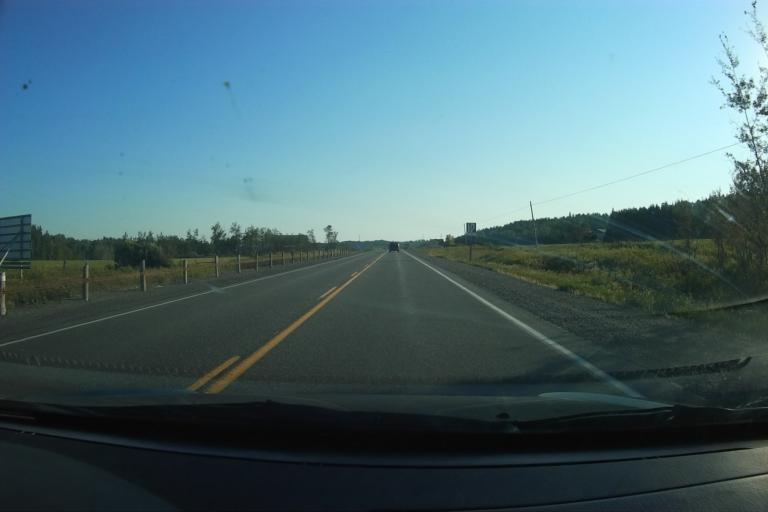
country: CA
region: Ontario
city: Temiskaming Shores
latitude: 47.4690
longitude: -79.7154
